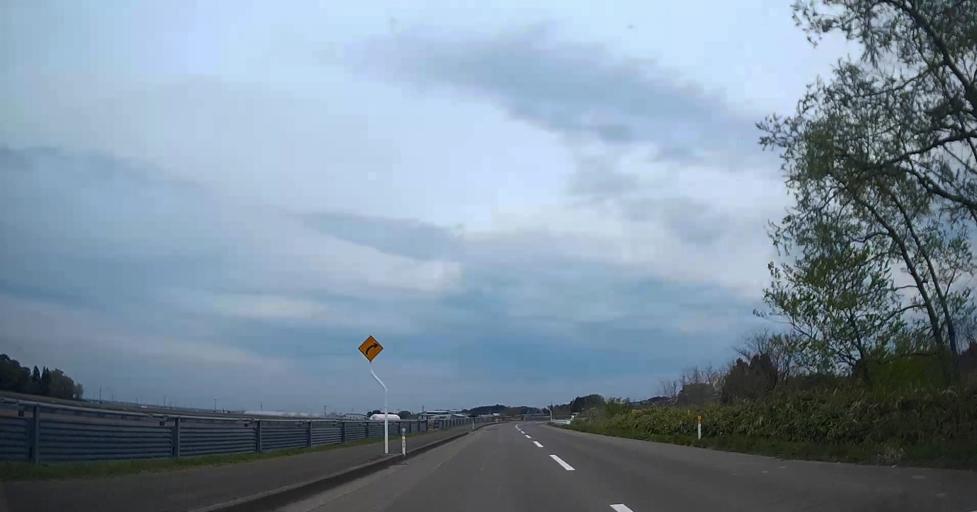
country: JP
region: Aomori
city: Goshogawara
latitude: 40.8988
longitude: 140.4828
